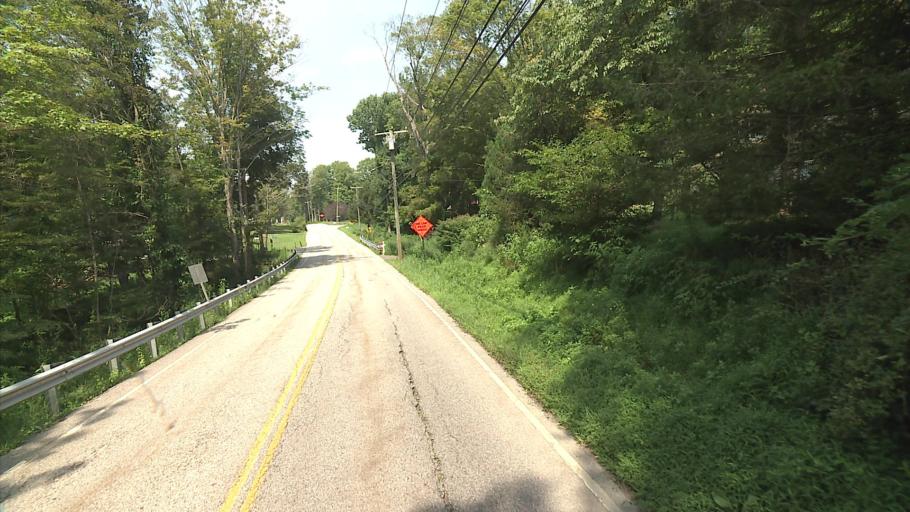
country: US
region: Connecticut
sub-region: Middlesex County
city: Chester Center
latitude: 41.4302
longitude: -72.4052
